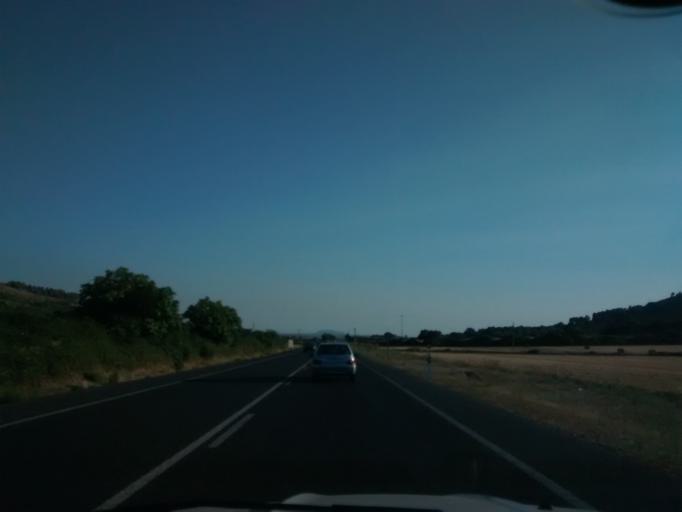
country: ES
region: Balearic Islands
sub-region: Illes Balears
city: Alcudia
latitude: 39.8267
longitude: 3.0609
